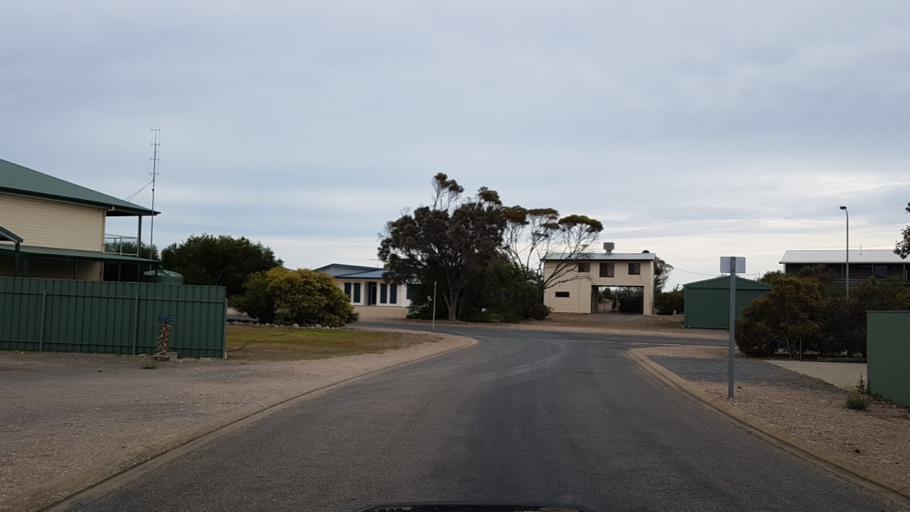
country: AU
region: South Australia
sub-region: Yorke Peninsula
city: Port Victoria
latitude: -34.9082
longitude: 137.0515
